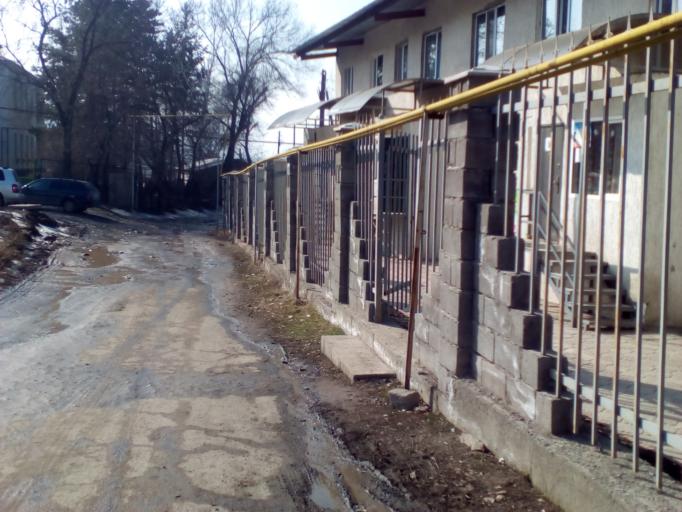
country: KZ
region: Almaty Oblysy
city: Burunday
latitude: 43.1585
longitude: 76.4135
